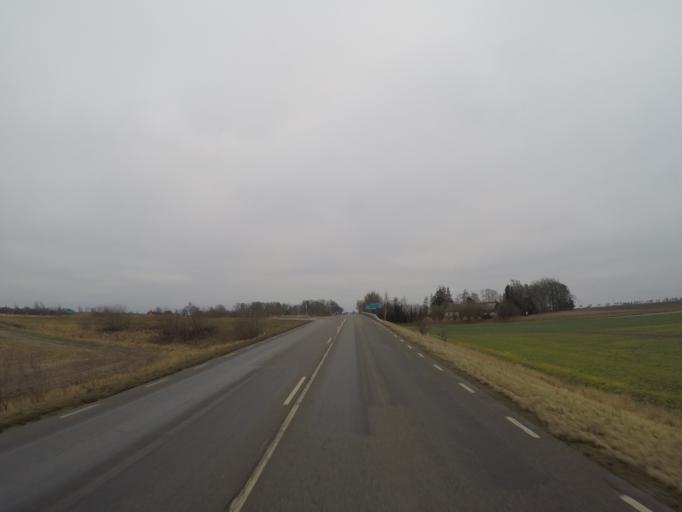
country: SE
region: Skane
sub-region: Hoors Kommun
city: Loberod
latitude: 55.7860
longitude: 13.4146
